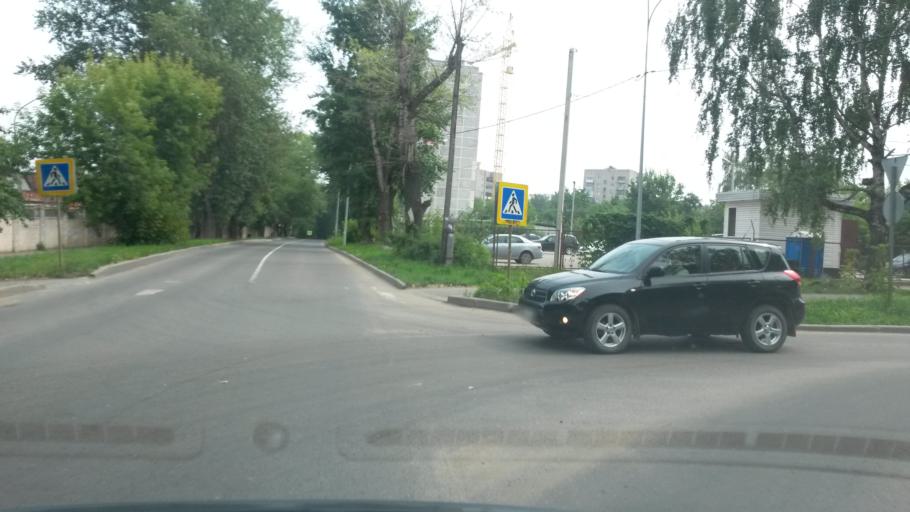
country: RU
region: Ivanovo
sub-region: Gorod Ivanovo
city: Ivanovo
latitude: 57.0064
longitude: 40.9602
